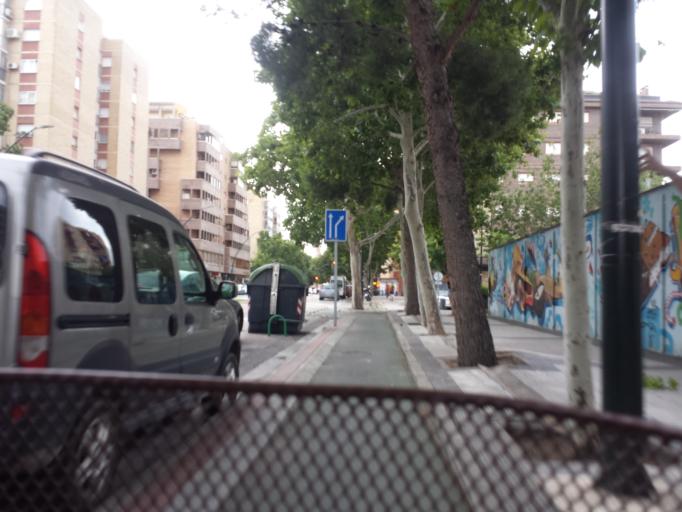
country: ES
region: Aragon
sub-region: Provincia de Zaragoza
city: Zaragoza
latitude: 41.6628
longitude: -0.8726
